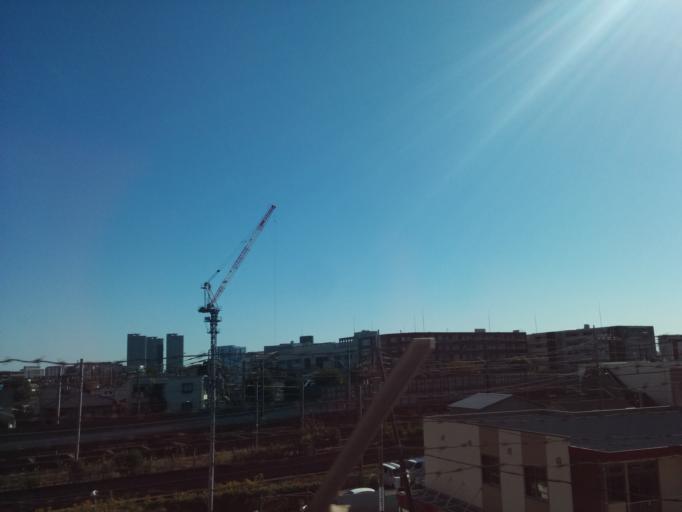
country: JP
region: Kanagawa
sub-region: Kawasaki-shi
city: Kawasaki
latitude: 35.5683
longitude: 139.6645
